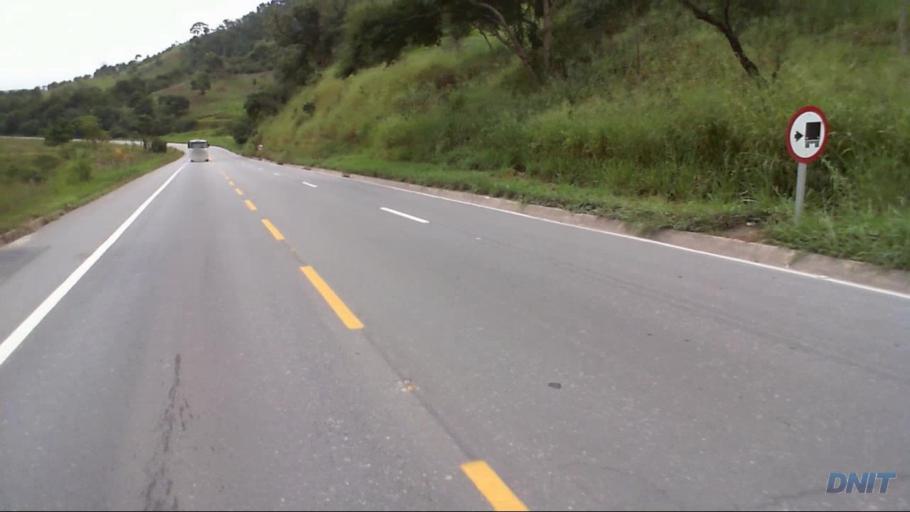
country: BR
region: Minas Gerais
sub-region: Nova Era
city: Nova Era
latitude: -19.7154
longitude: -43.0013
